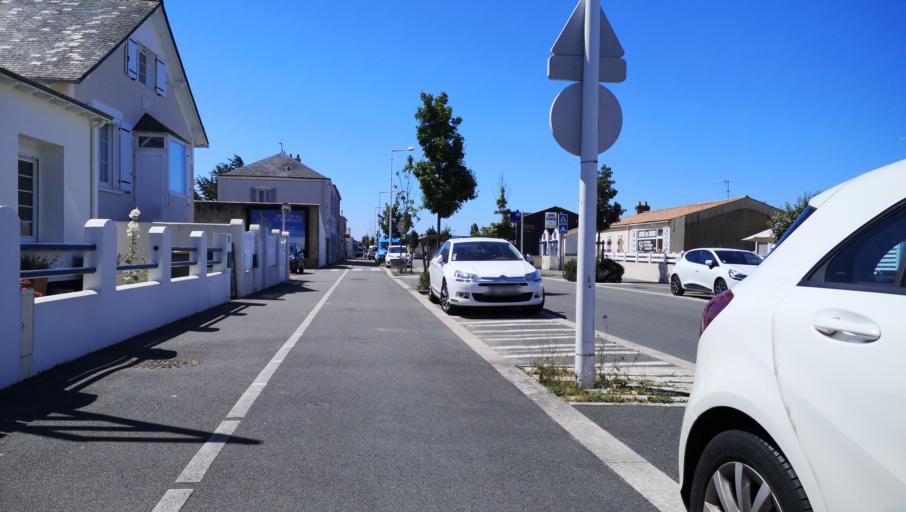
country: FR
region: Pays de la Loire
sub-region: Departement de la Vendee
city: Les Sables-d'Olonne
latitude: 46.5116
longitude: -1.7767
